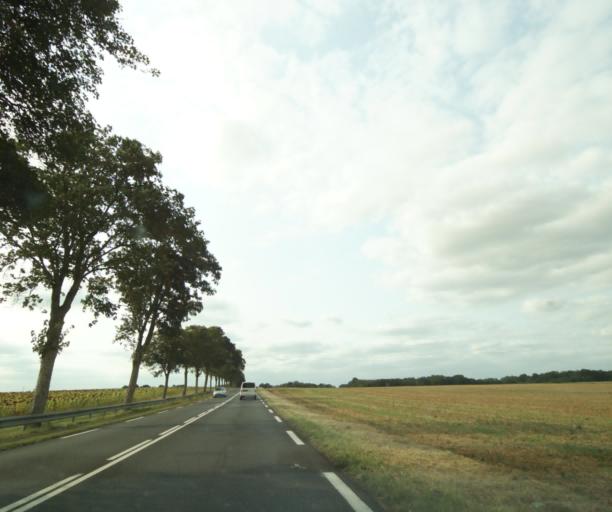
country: FR
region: Centre
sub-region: Departement d'Indre-et-Loire
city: Reignac-sur-Indre
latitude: 47.2276
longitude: 0.8792
